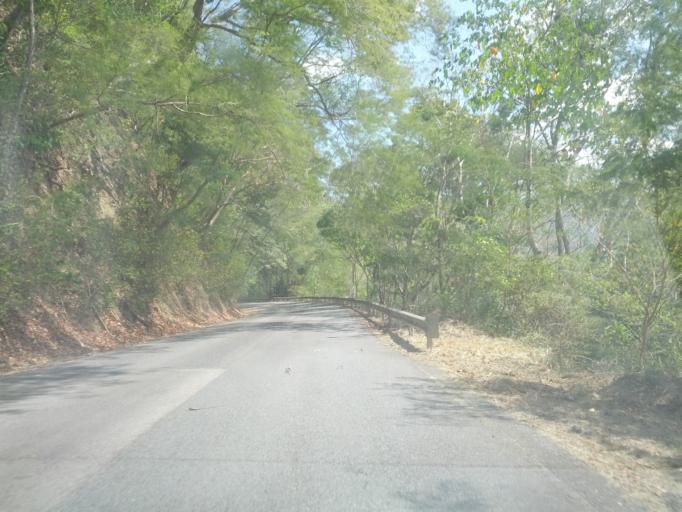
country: CR
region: Puntarenas
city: Ciudad Cortes
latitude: 8.9637
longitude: -83.3200
